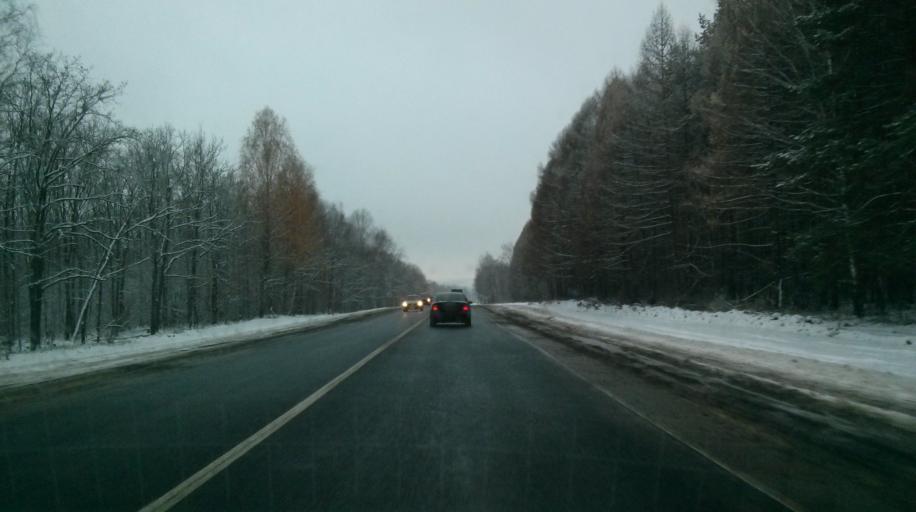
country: RU
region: Nizjnij Novgorod
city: Vorsma
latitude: 56.0013
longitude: 43.3125
